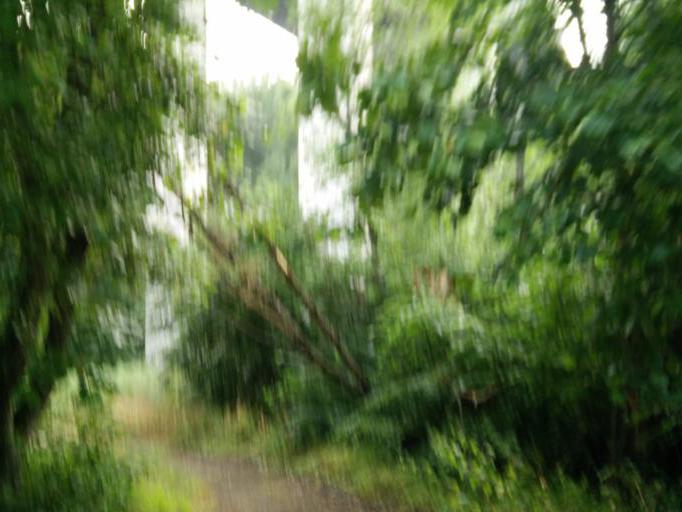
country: LU
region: Luxembourg
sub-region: Canton de Luxembourg
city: Bertrange
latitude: 49.6303
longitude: 6.0470
